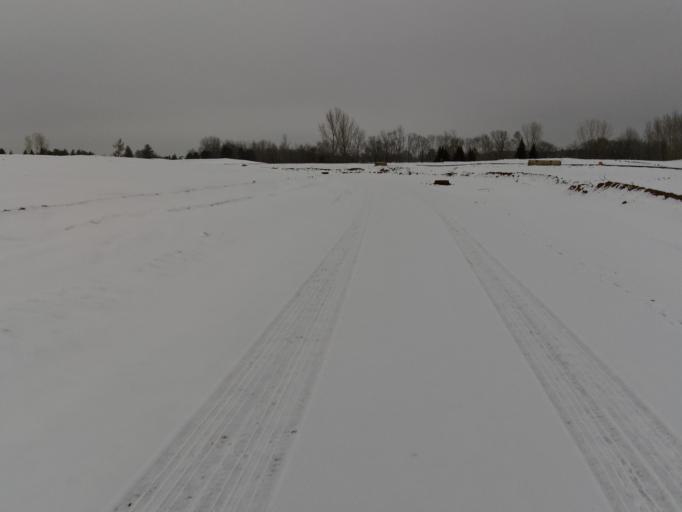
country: US
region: Minnesota
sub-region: Washington County
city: Lake Elmo
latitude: 44.9663
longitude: -92.8700
